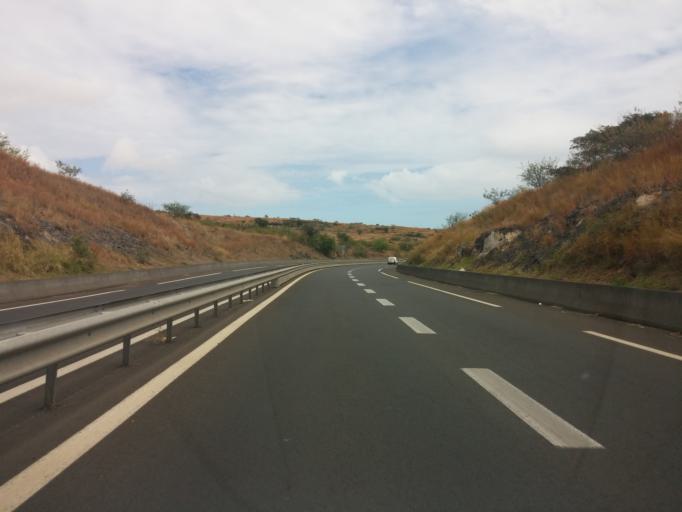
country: RE
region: Reunion
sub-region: Reunion
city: Saint-Paul
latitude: -21.0196
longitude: 55.2630
